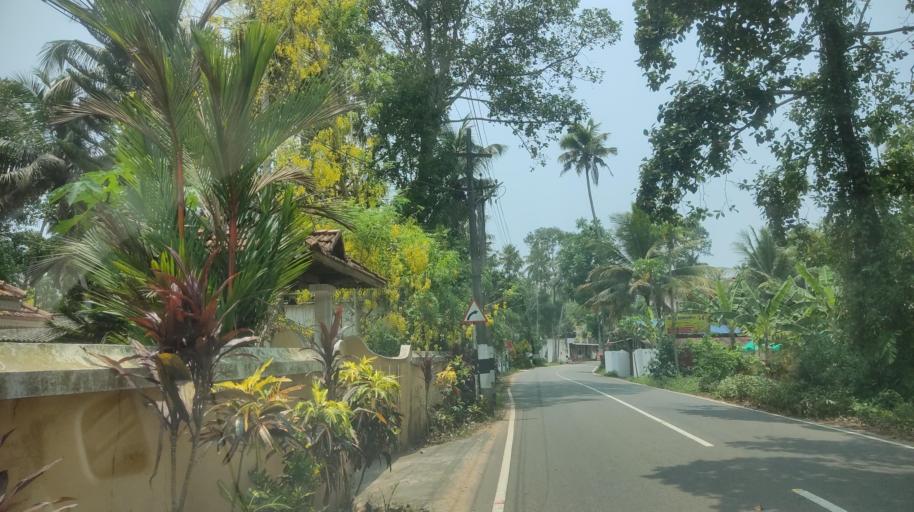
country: IN
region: Kerala
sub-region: Alappuzha
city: Shertallai
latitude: 9.6533
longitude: 76.3711
